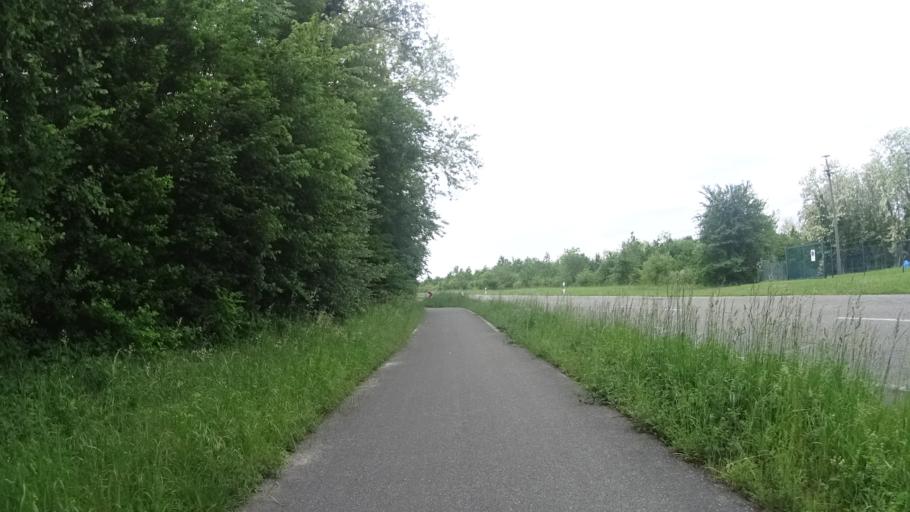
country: DE
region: Baden-Wuerttemberg
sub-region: Freiburg Region
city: Neuenburg am Rhein
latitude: 47.7824
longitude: 7.5542
